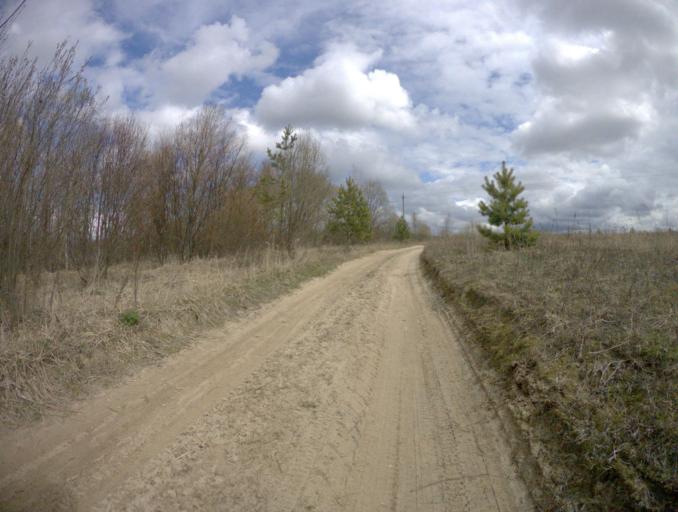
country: RU
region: Vladimir
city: Orgtrud
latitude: 56.0682
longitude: 40.6860
